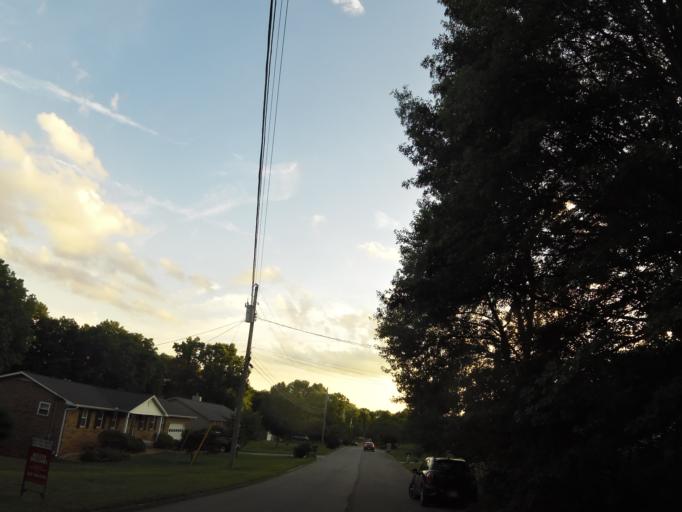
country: US
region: Tennessee
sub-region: Knox County
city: Farragut
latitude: 35.9278
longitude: -84.1445
